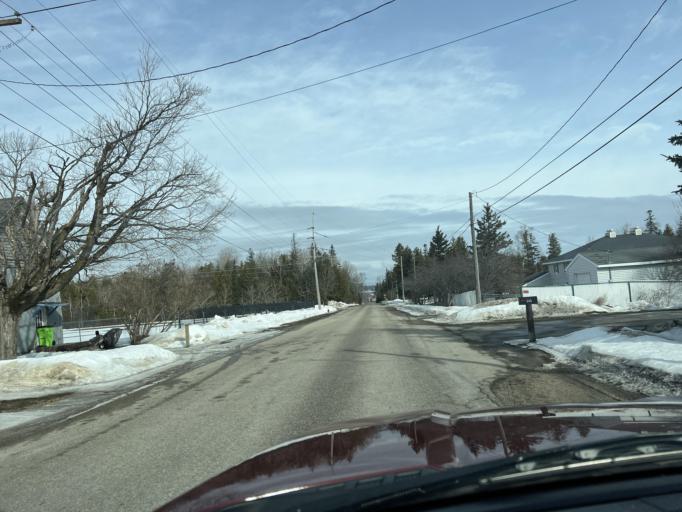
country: US
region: Michigan
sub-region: Mackinac County
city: Saint Ignace
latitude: 45.8606
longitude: -84.7235
